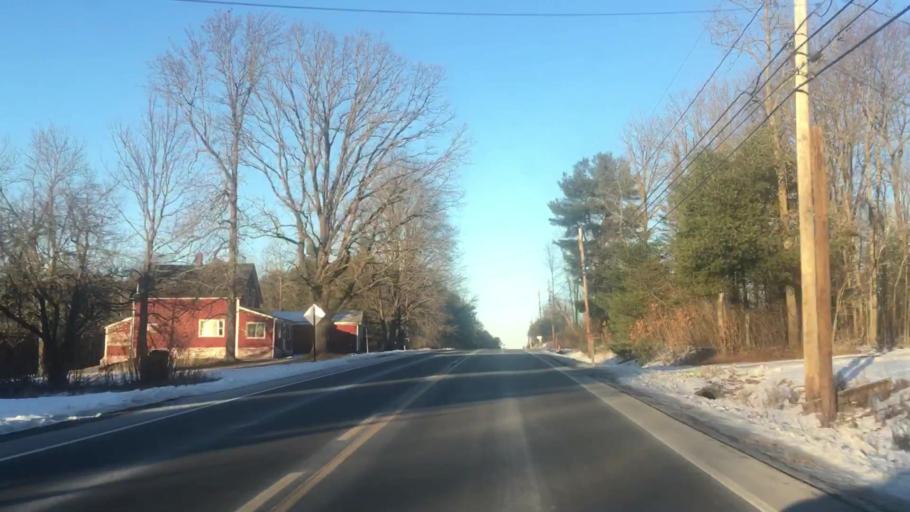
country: US
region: Maine
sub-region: Kennebec County
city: Benton
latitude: 44.5862
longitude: -69.5458
